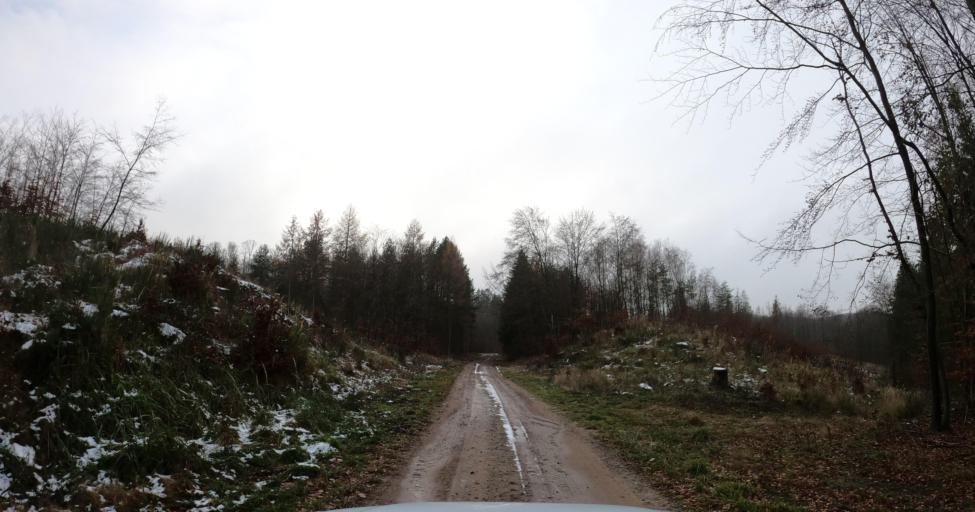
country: PL
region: West Pomeranian Voivodeship
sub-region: Powiat swidwinski
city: Rabino
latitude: 53.8936
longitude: 15.8938
